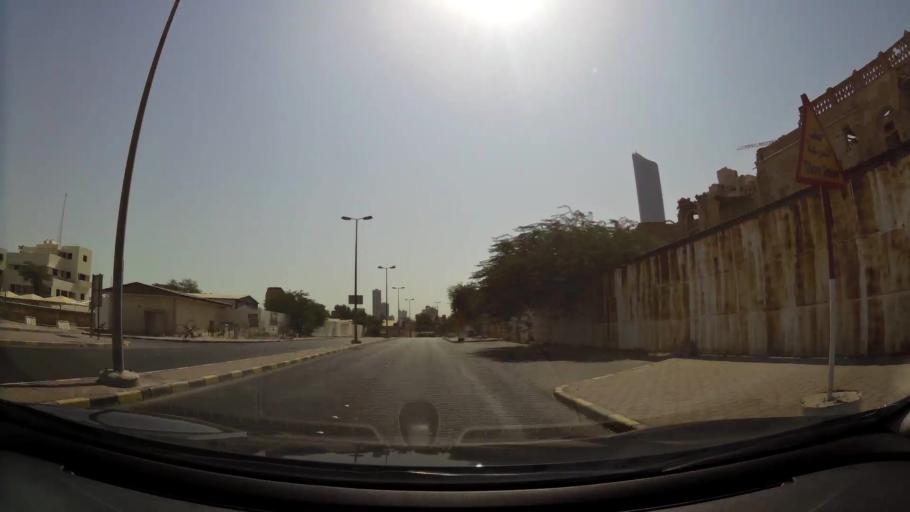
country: KW
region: Al Asimah
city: Ad Dasmah
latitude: 29.3886
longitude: 47.9946
